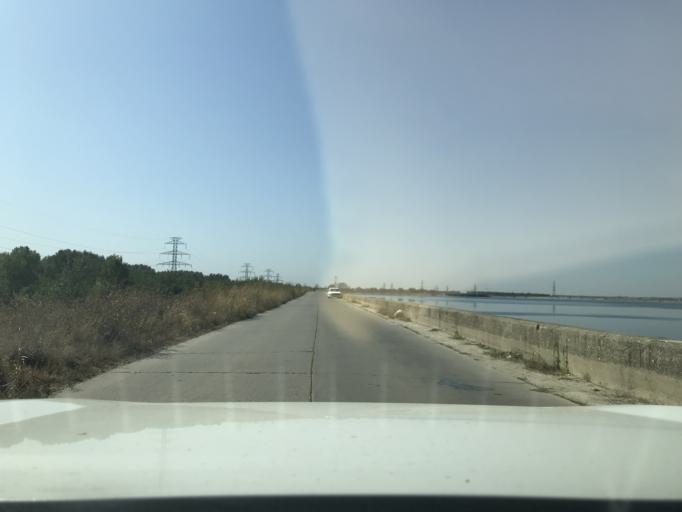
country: RO
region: Olt
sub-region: Municipiul Slatina
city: Slatina
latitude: 44.4021
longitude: 24.3558
